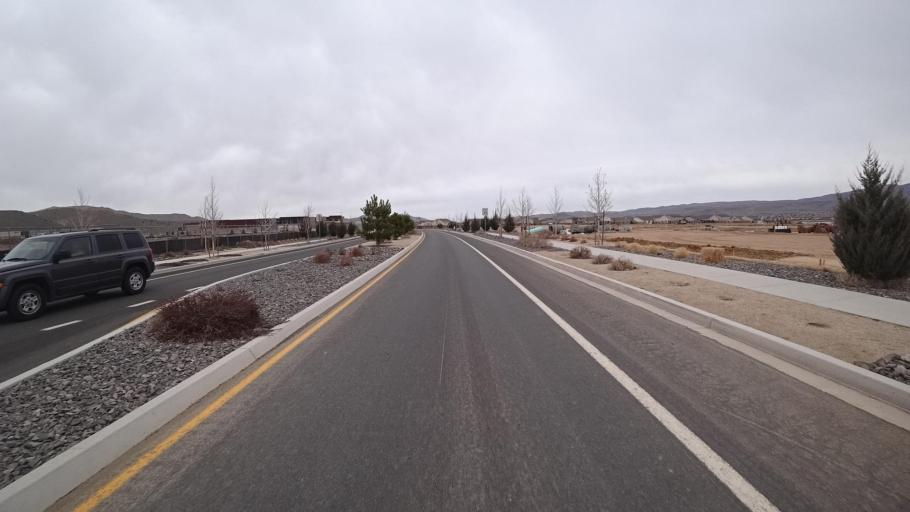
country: US
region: Nevada
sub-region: Washoe County
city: Spanish Springs
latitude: 39.6066
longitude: -119.7202
